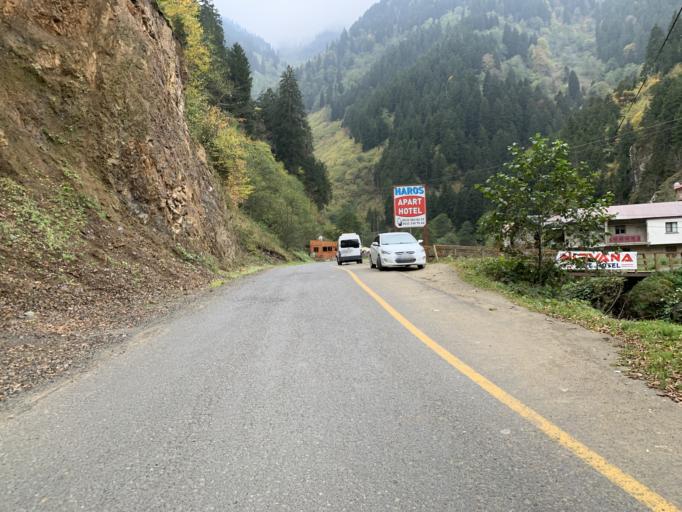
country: TR
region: Trabzon
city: Uzungol
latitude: 40.5963
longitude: 40.3215
